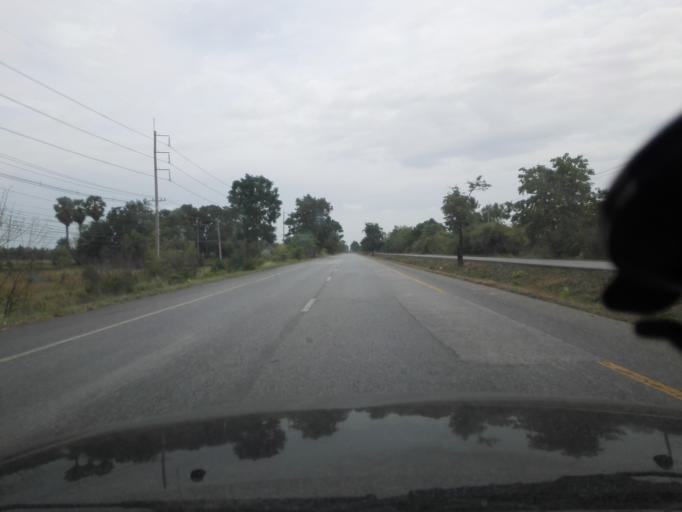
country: TH
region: Kamphaeng Phet
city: Khlong Khlung
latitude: 16.1188
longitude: 99.7195
